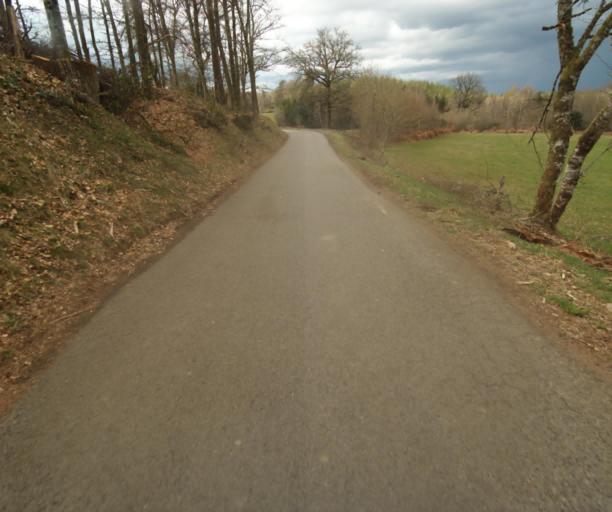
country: FR
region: Limousin
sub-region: Departement de la Correze
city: Egletons
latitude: 45.2623
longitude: 1.9894
